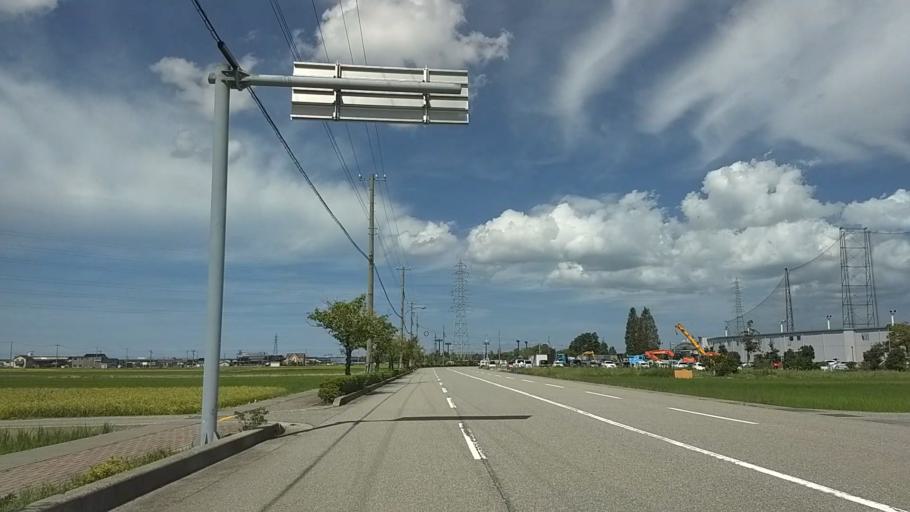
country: JP
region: Ishikawa
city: Kanazawa-shi
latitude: 36.5908
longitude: 136.6563
